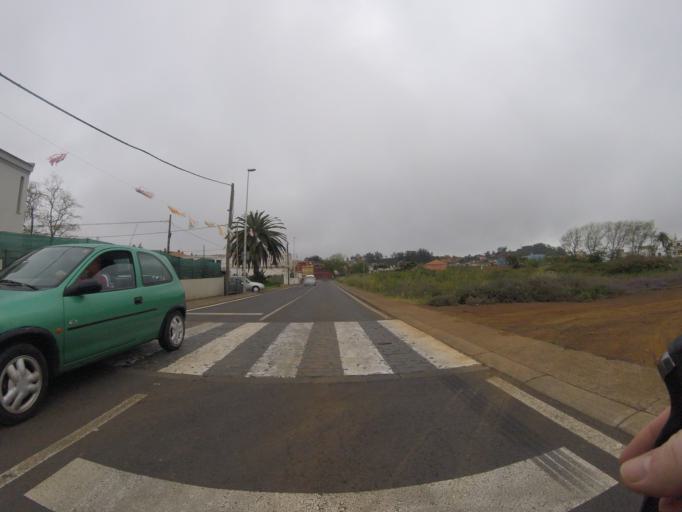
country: ES
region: Canary Islands
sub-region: Provincia de Santa Cruz de Tenerife
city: Tacoronte
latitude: 28.4942
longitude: -16.3762
